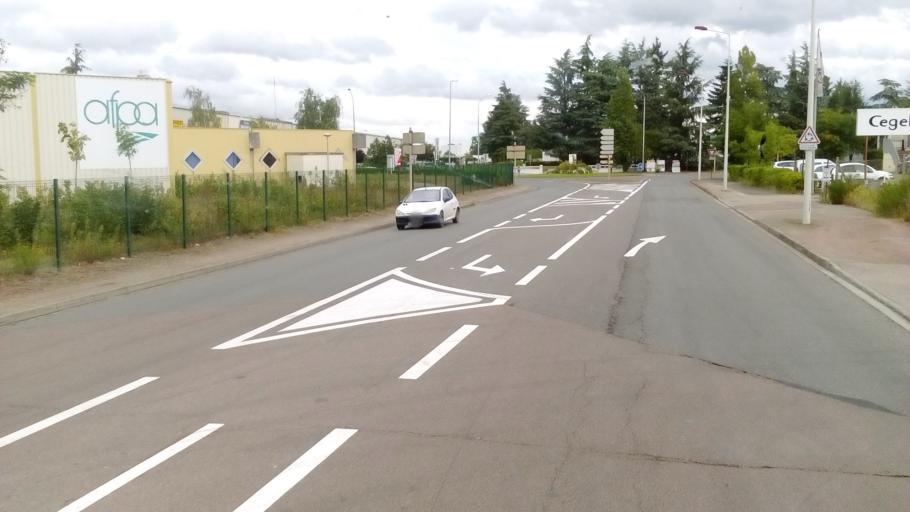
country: FR
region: Rhone-Alpes
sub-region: Departement de la Loire
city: Roanne
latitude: 46.0542
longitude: 4.0797
